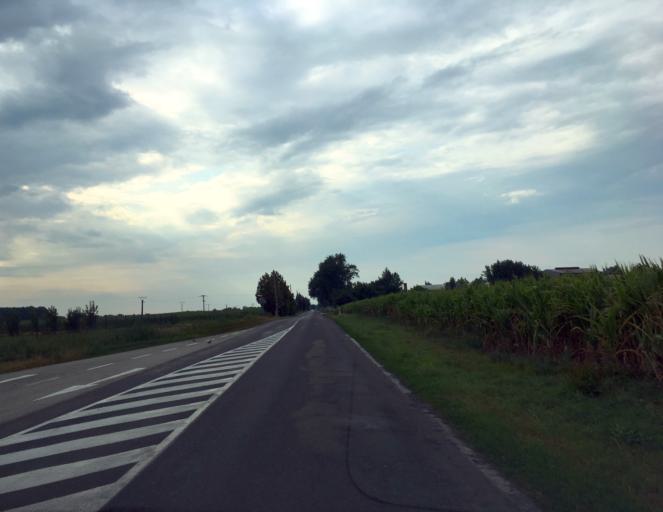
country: SK
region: Trnavsky
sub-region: Okres Dunajska Streda
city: Velky Meder
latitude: 47.9295
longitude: 17.7300
